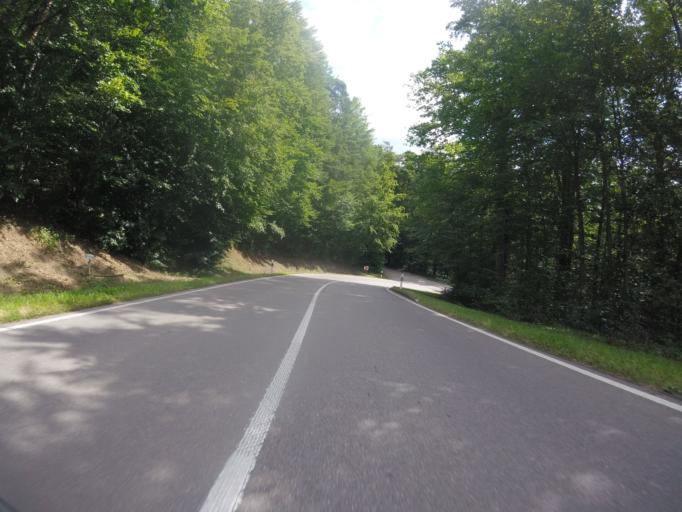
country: DE
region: Baden-Wuerttemberg
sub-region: Regierungsbezirk Stuttgart
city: Winnenden
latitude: 48.8290
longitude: 9.4119
